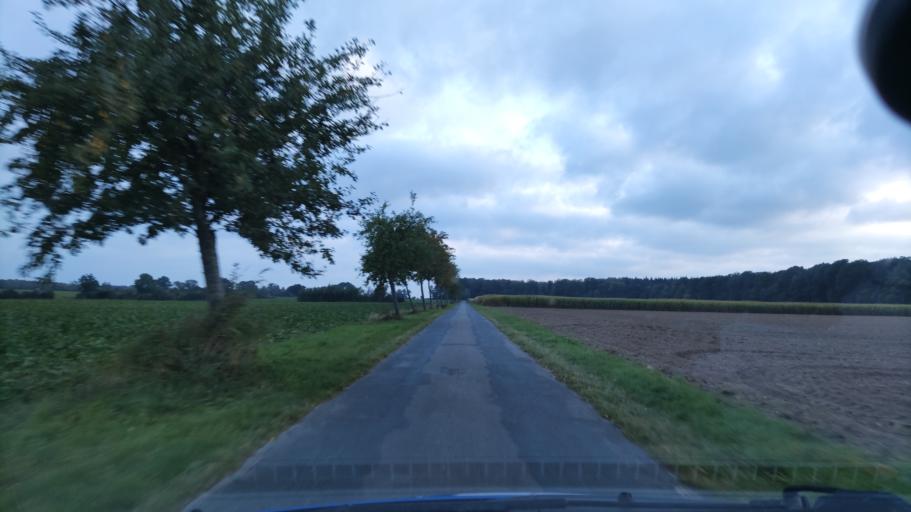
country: DE
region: Lower Saxony
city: Tosterglope
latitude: 53.2305
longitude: 10.8297
